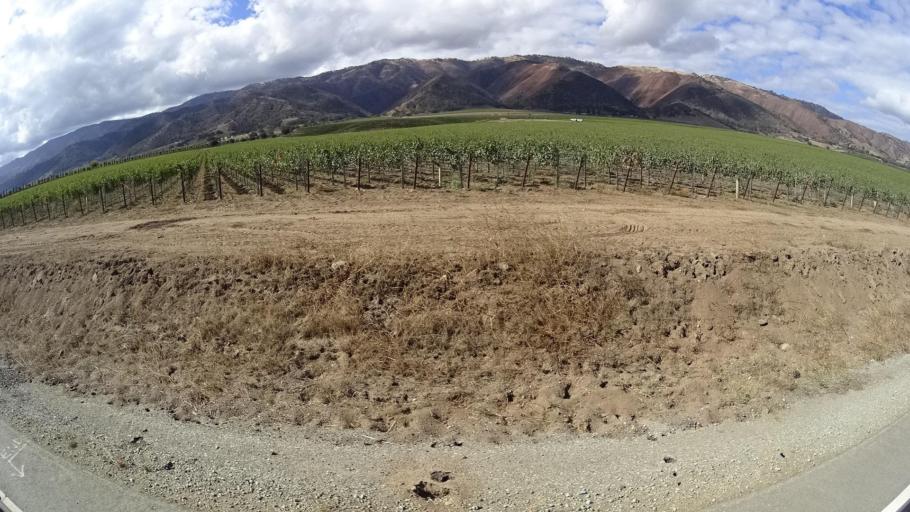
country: US
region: California
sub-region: Monterey County
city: Gonzales
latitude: 36.4909
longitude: -121.4900
